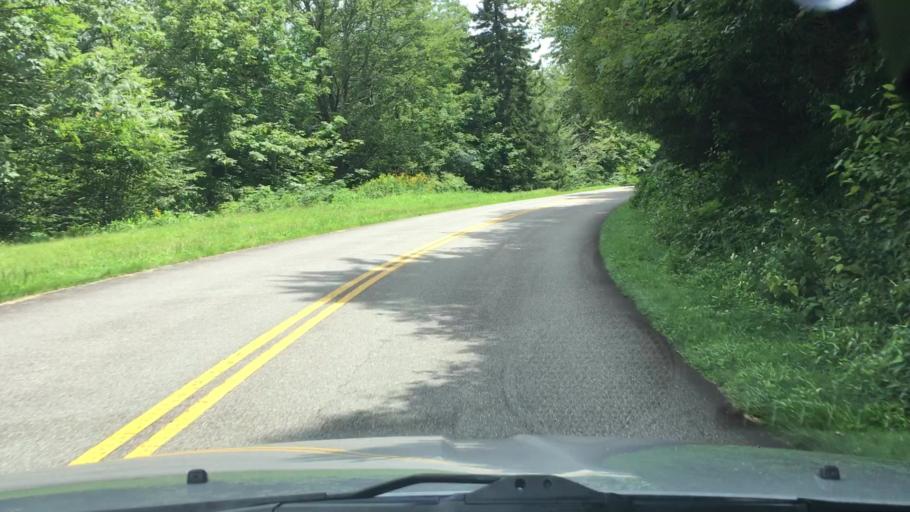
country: US
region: North Carolina
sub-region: Buncombe County
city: Black Mountain
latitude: 35.7075
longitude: -82.2635
